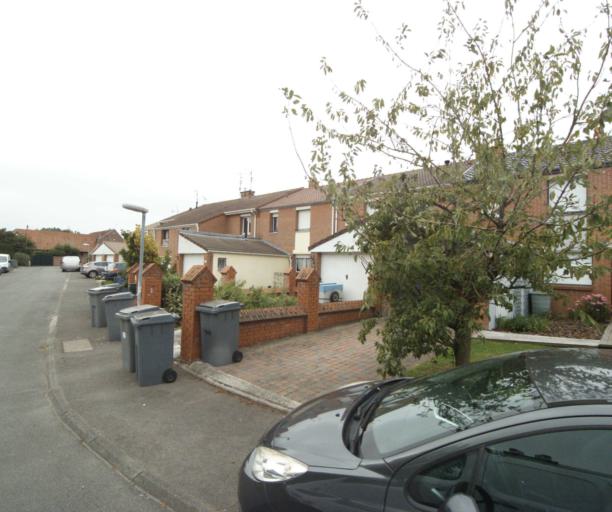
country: FR
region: Nord-Pas-de-Calais
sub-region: Departement du Nord
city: Willems
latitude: 50.6117
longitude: 3.2309
